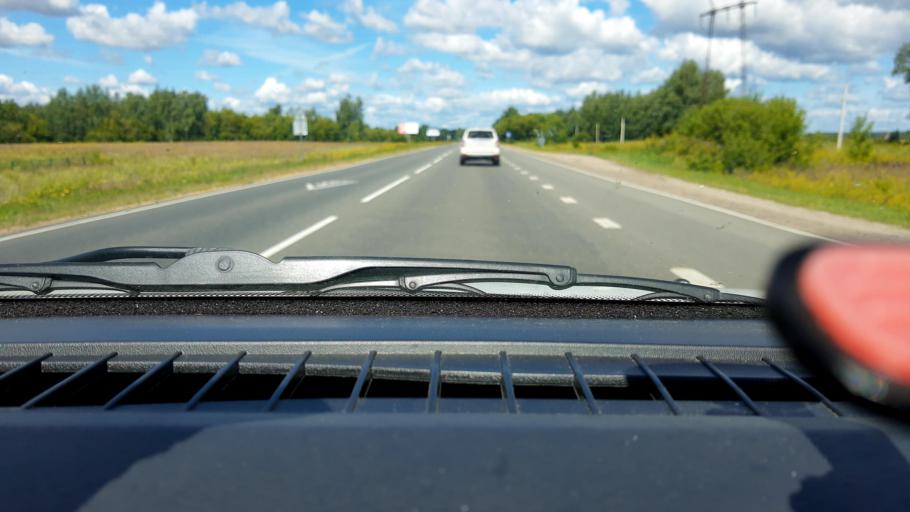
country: RU
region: Nizjnij Novgorod
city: Arzamas
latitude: 55.3113
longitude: 43.9035
